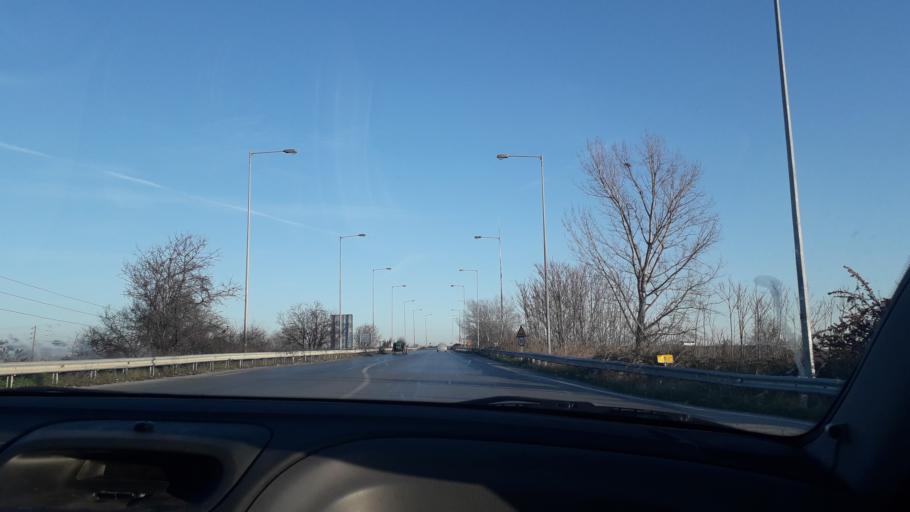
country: GR
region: Central Macedonia
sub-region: Nomos Imathias
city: Agkathia
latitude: 40.5908
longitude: 22.4679
